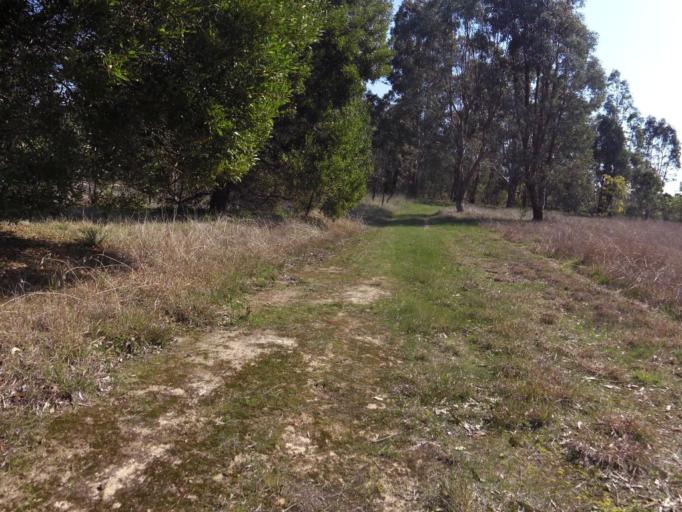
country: AU
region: Victoria
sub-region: Murrindindi
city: Alexandra
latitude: -36.9783
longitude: 145.7115
